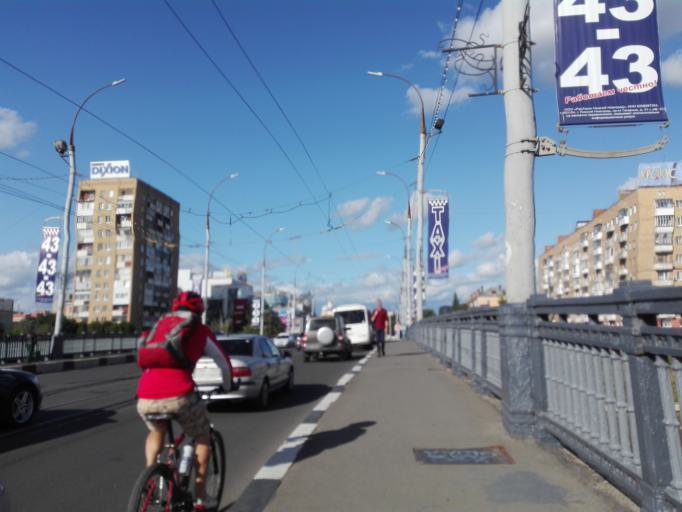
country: RU
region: Orjol
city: Orel
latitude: 52.9658
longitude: 36.0720
